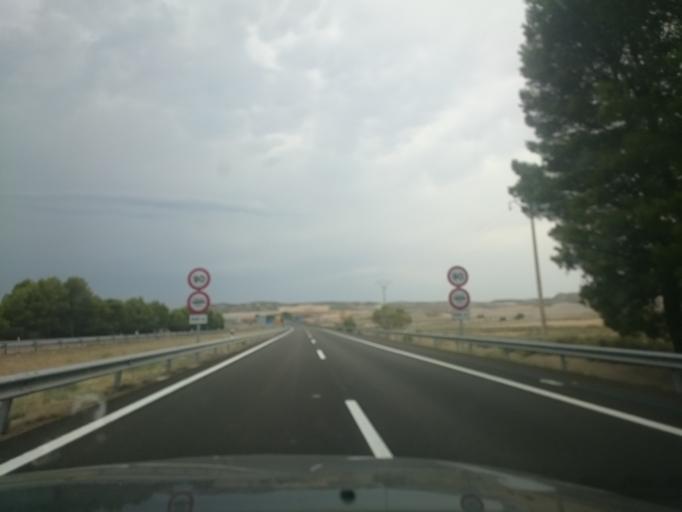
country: ES
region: Aragon
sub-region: Provincia de Zaragoza
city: Pina de Ebro
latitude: 41.5250
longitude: -0.4604
